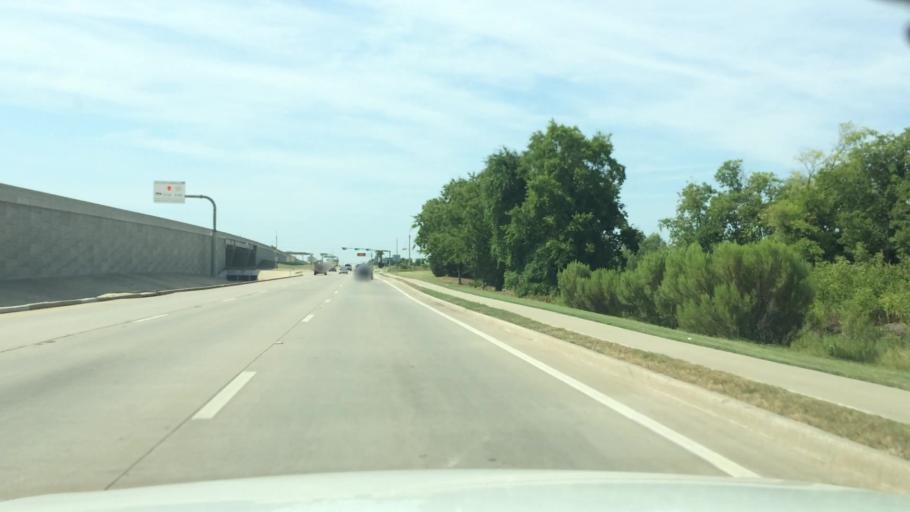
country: US
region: Texas
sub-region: Dallas County
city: Grand Prairie
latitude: 32.7076
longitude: -97.0253
